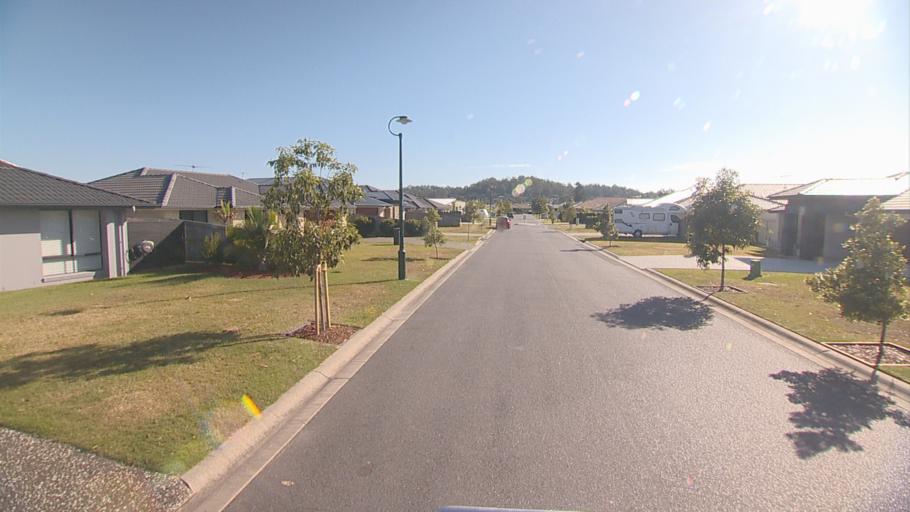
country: AU
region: Queensland
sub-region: Logan
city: Waterford West
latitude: -27.6867
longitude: 153.1719
